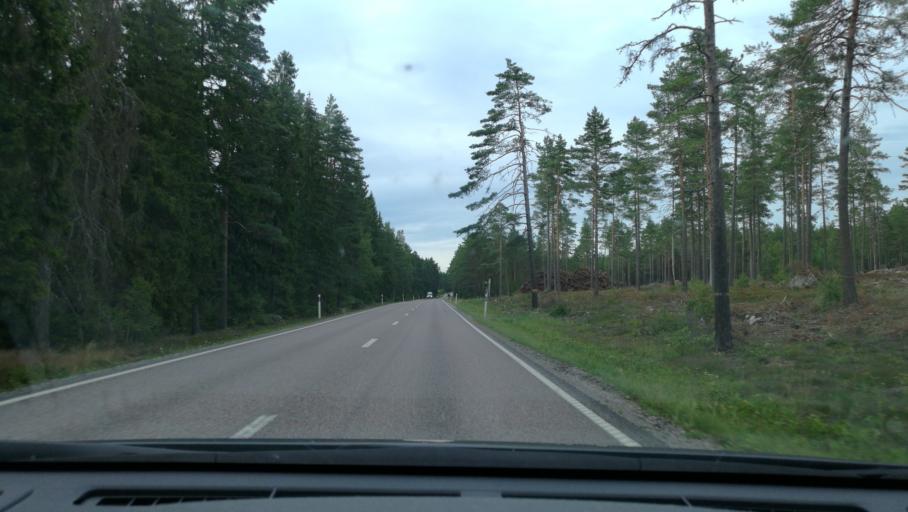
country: SE
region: Vaestmanland
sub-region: Kungsors Kommun
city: Kungsoer
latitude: 59.3208
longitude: 16.1099
